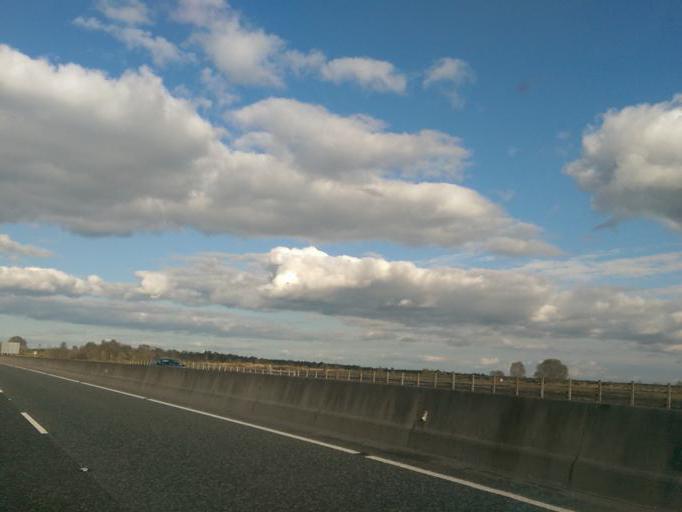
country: IE
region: Leinster
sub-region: An Iarmhi
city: Rochfortbridge
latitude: 53.4234
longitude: -7.2391
